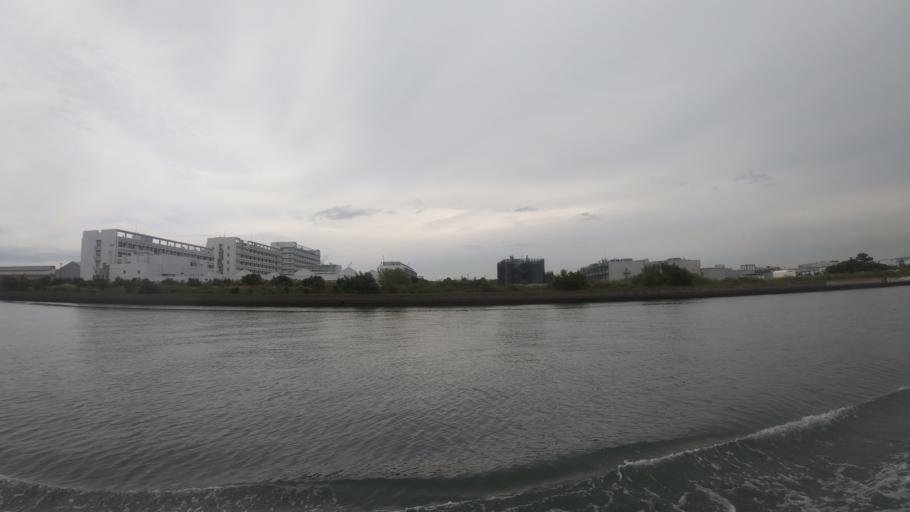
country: JP
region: Kanagawa
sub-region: Kawasaki-shi
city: Kawasaki
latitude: 35.4871
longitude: 139.6797
